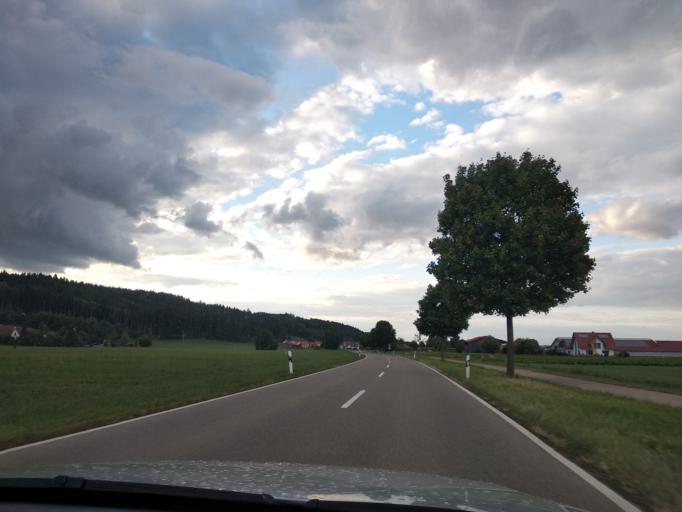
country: DE
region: Bavaria
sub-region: Swabia
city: Woringen
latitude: 47.9095
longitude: 10.2049
